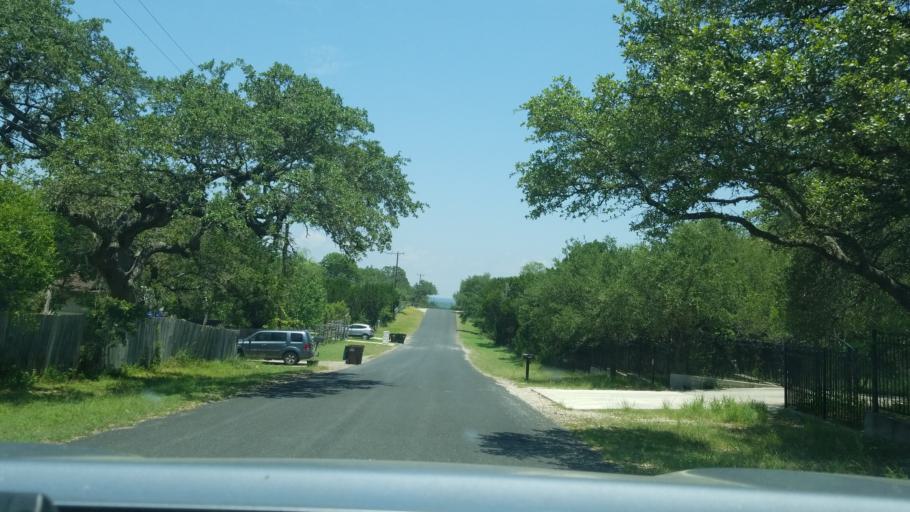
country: US
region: Texas
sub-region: Bexar County
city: Timberwood Park
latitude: 29.7002
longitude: -98.5162
